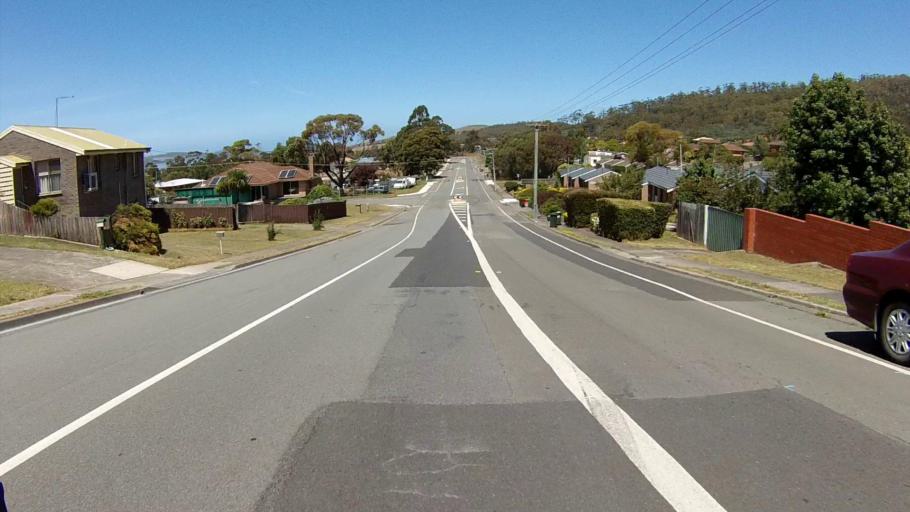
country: AU
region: Tasmania
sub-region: Clarence
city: Rokeby
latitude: -42.8932
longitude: 147.4314
